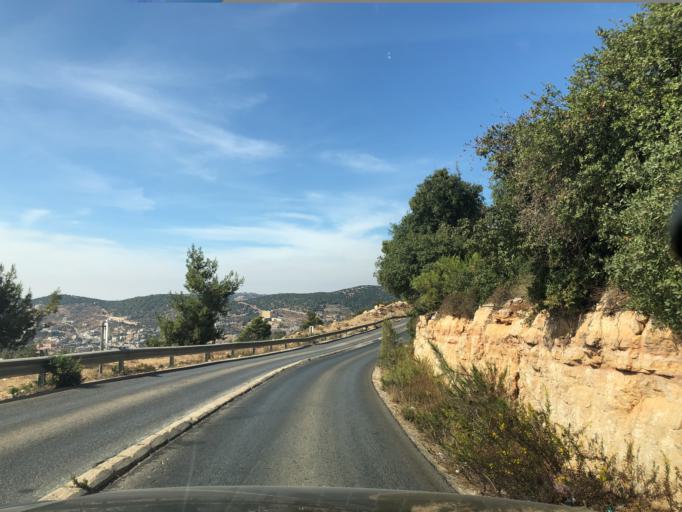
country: JO
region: Irbid
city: `Ayn Jannah
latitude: 32.3210
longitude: 35.7610
